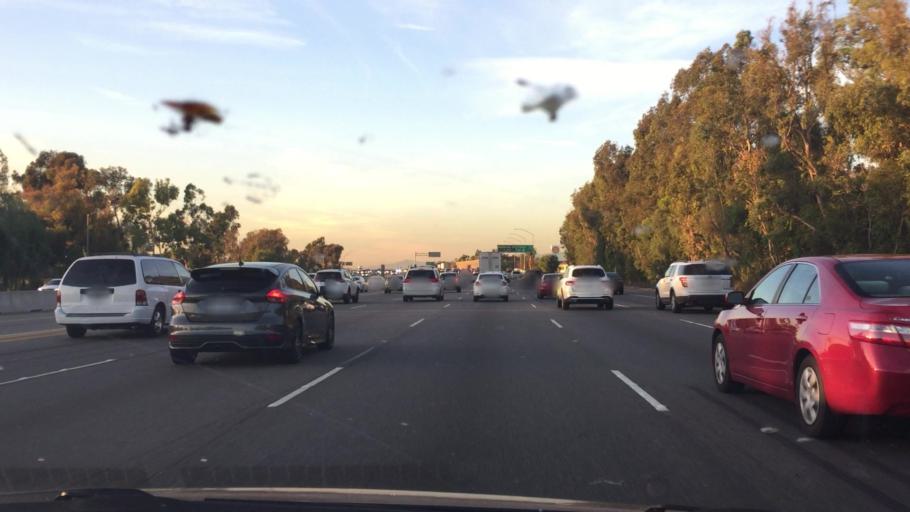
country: US
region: California
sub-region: Orange County
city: Irvine
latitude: 33.7050
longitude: -117.7780
